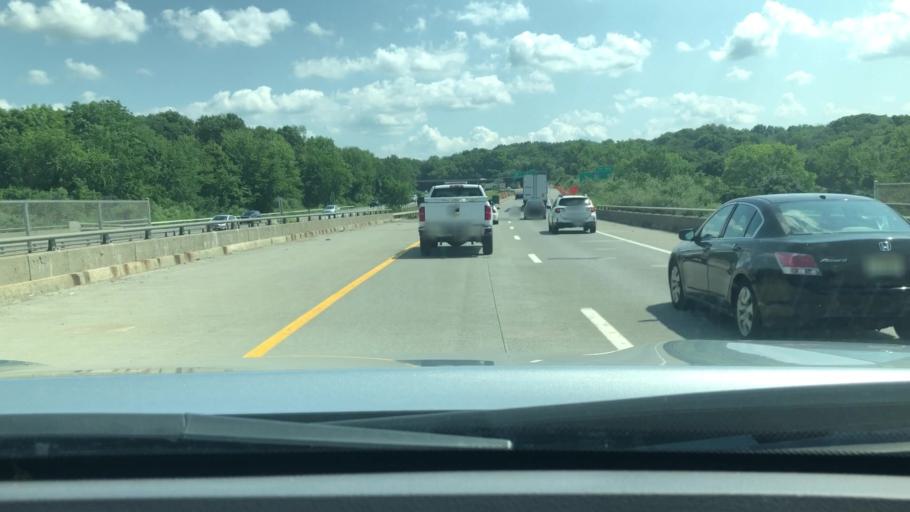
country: US
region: New York
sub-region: Putnam County
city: Brewster
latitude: 41.3972
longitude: -73.6009
